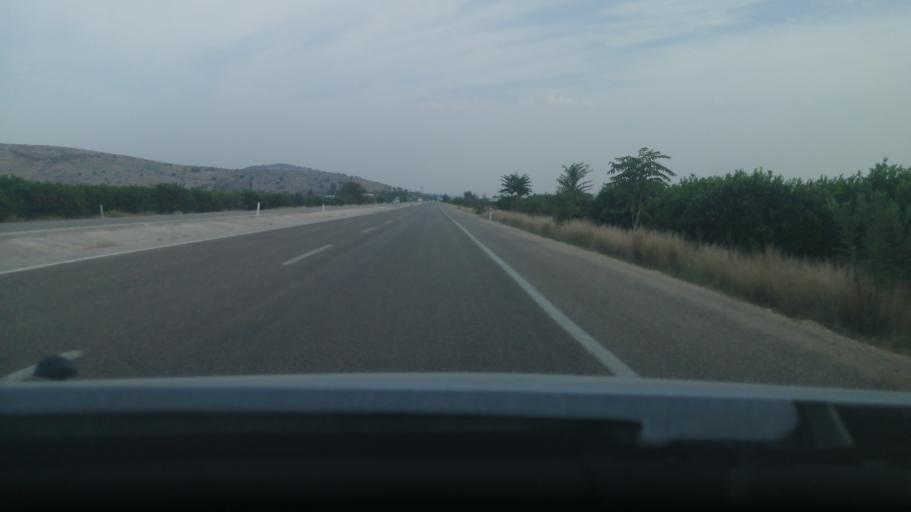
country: TR
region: Adana
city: Kozan
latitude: 37.3836
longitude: 35.8131
